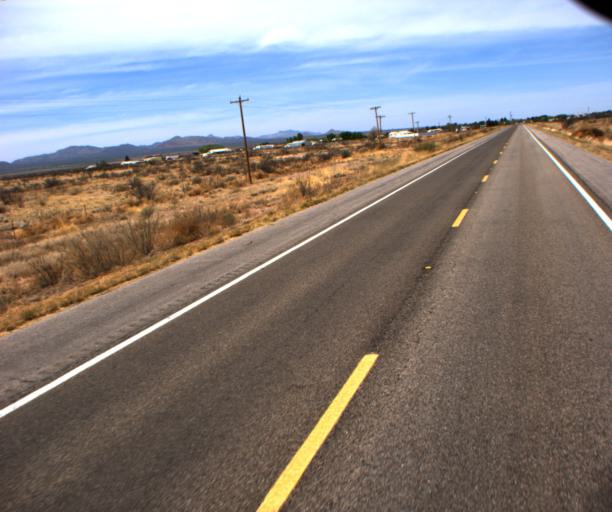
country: US
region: Arizona
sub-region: Cochise County
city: Pirtleville
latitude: 31.6656
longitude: -109.6803
